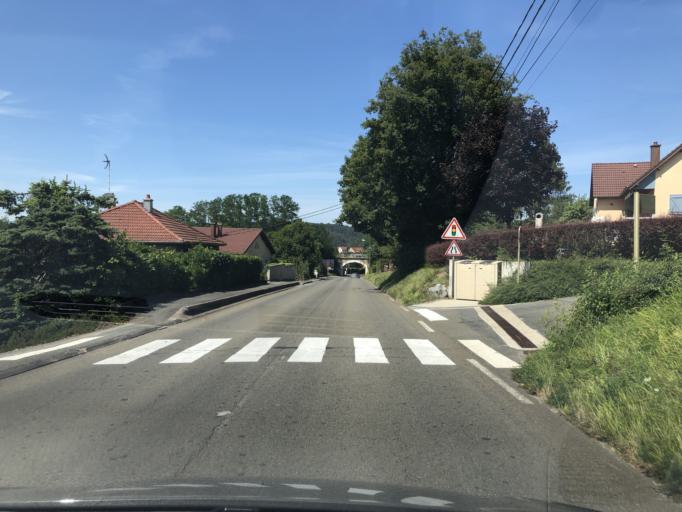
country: FR
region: Franche-Comte
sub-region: Departement du Doubs
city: Voujeaucourt
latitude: 47.4662
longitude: 6.7651
